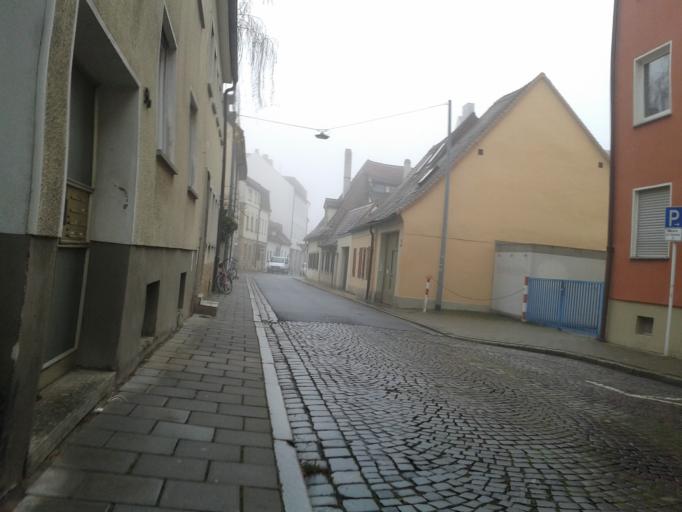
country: DE
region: Bavaria
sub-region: Upper Franconia
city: Bamberg
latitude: 49.8975
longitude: 10.8986
